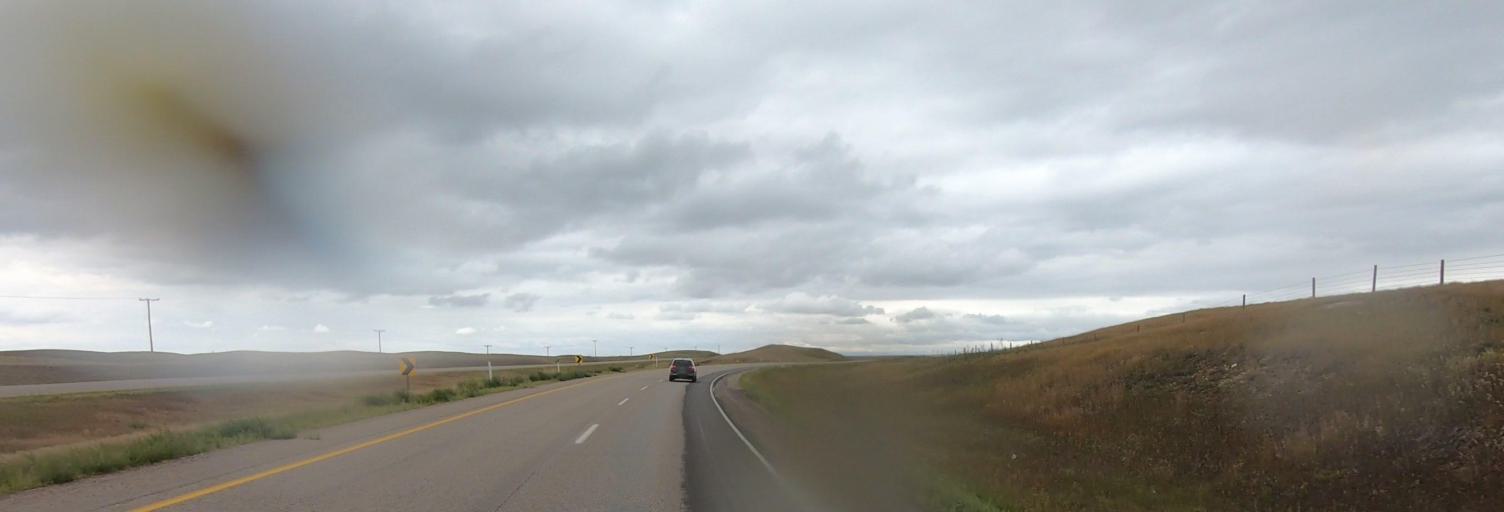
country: CA
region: Saskatchewan
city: Gravelbourg
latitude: 50.4631
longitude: -106.4929
